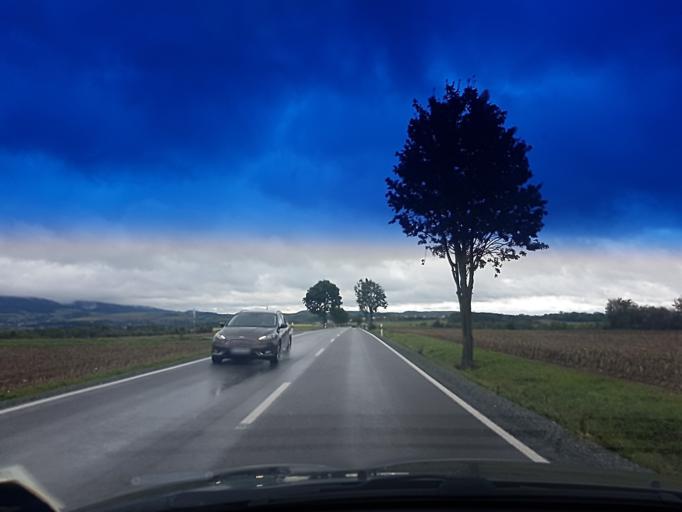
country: DE
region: Bavaria
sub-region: Upper Franconia
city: Bindlach
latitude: 50.0119
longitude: 11.6133
